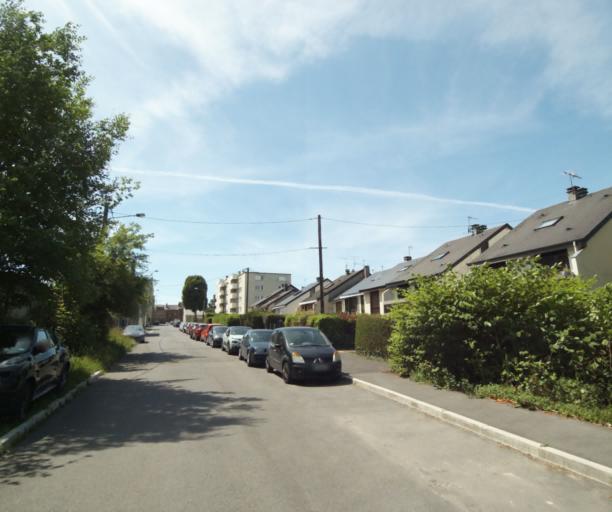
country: FR
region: Champagne-Ardenne
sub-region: Departement des Ardennes
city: Charleville-Mezieres
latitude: 49.7561
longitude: 4.7232
